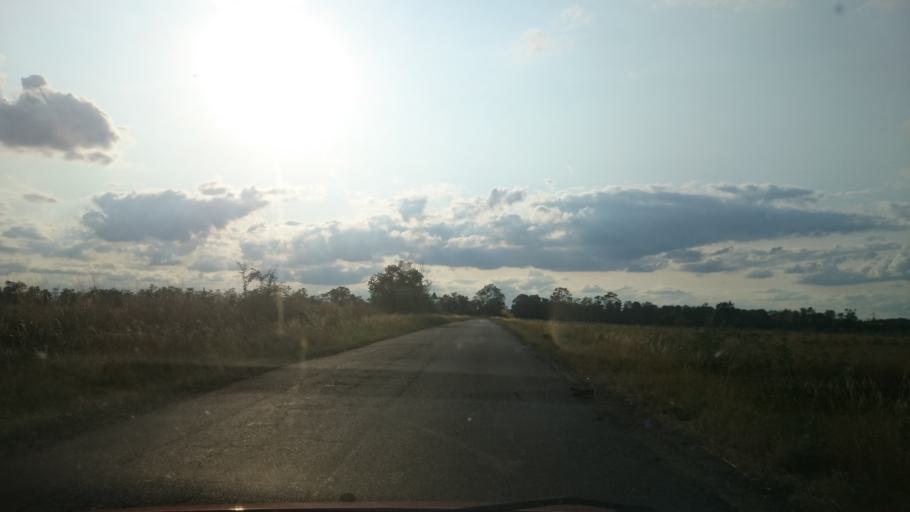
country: PL
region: Opole Voivodeship
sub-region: Powiat nyski
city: Otmuchow
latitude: 50.5066
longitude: 17.1633
